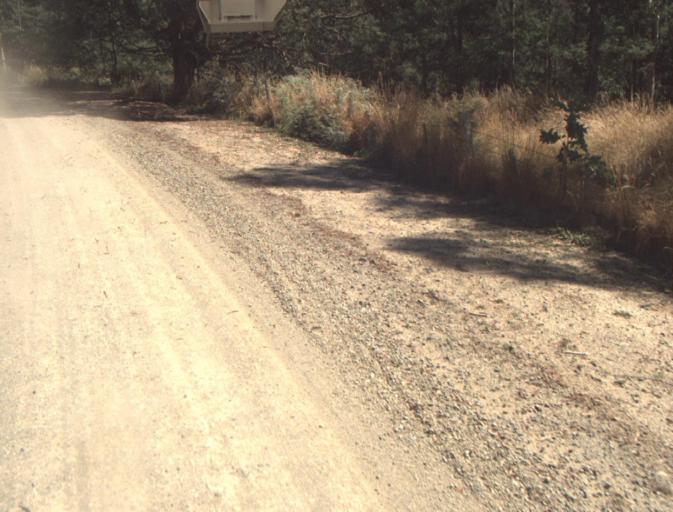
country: AU
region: Tasmania
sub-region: Dorset
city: Scottsdale
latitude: -41.3328
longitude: 147.4340
